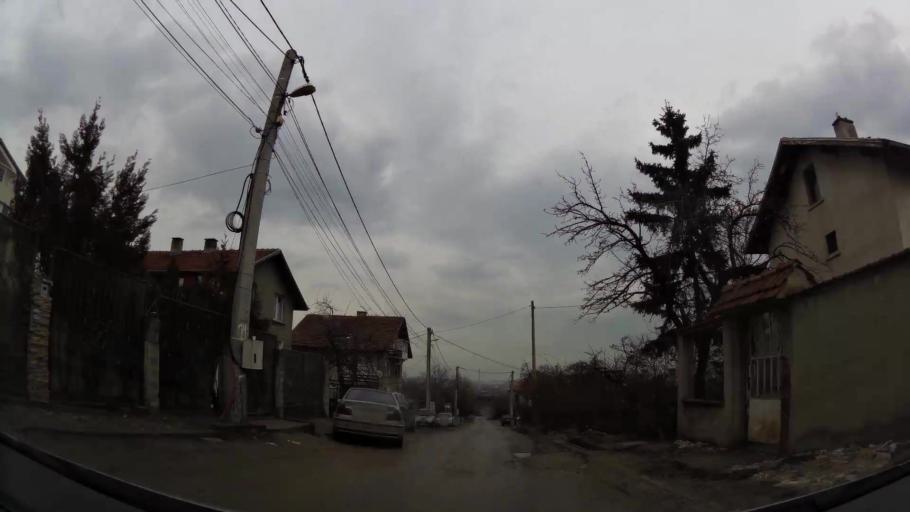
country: BG
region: Sofiya
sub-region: Obshtina Bozhurishte
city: Bozhurishte
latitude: 42.6840
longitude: 23.2344
